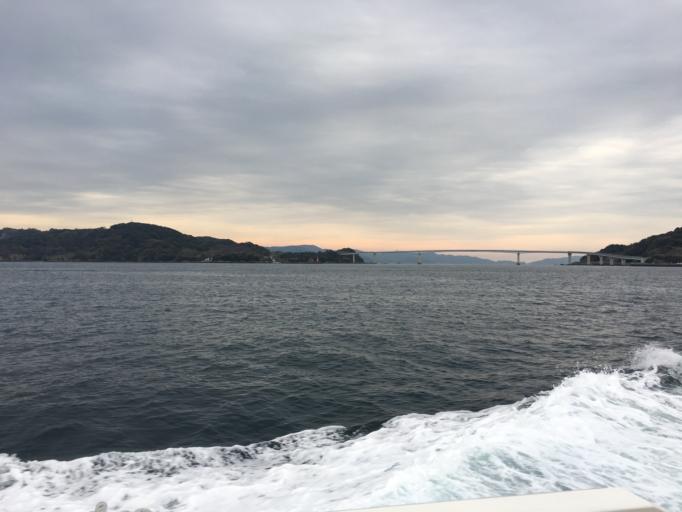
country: JP
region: Nagasaki
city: Nagasaki-shi
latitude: 32.7051
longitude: 129.7900
